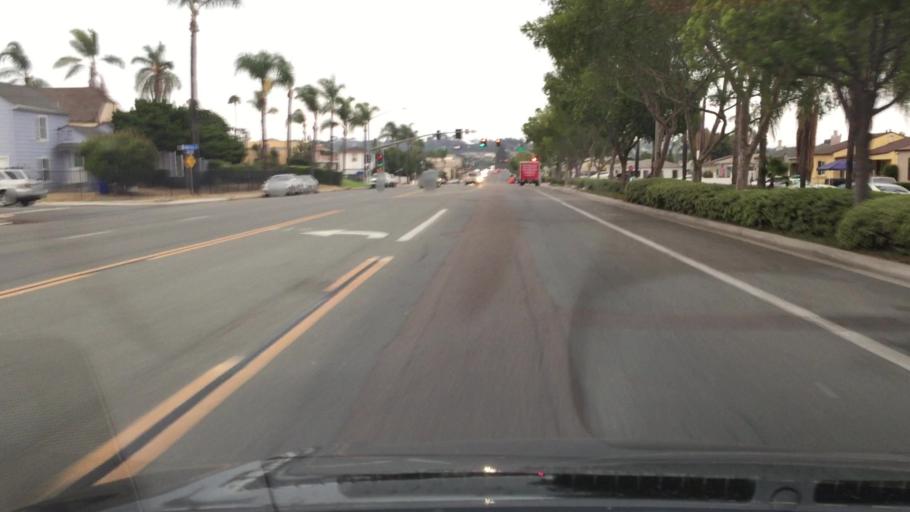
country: US
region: California
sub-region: San Diego County
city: National City
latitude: 32.7214
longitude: -117.0913
